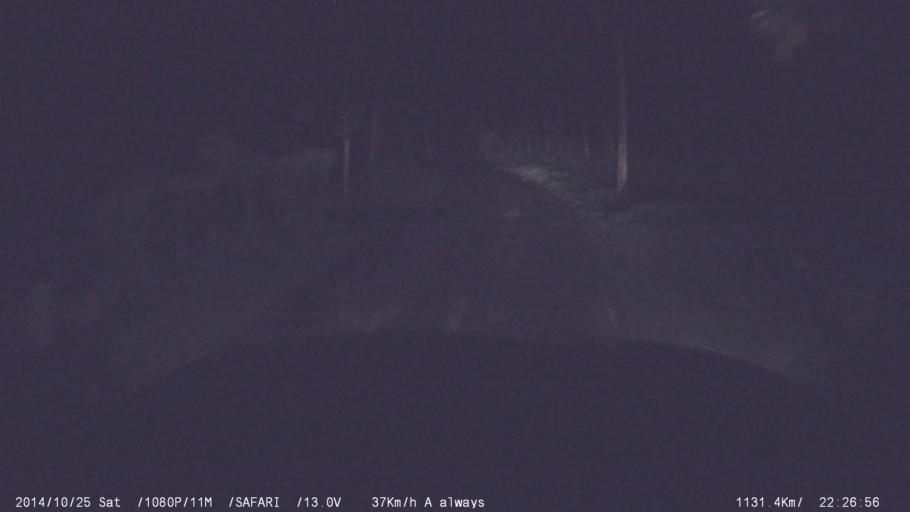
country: IN
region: Kerala
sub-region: Kottayam
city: Palackattumala
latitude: 9.7829
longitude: 76.5610
